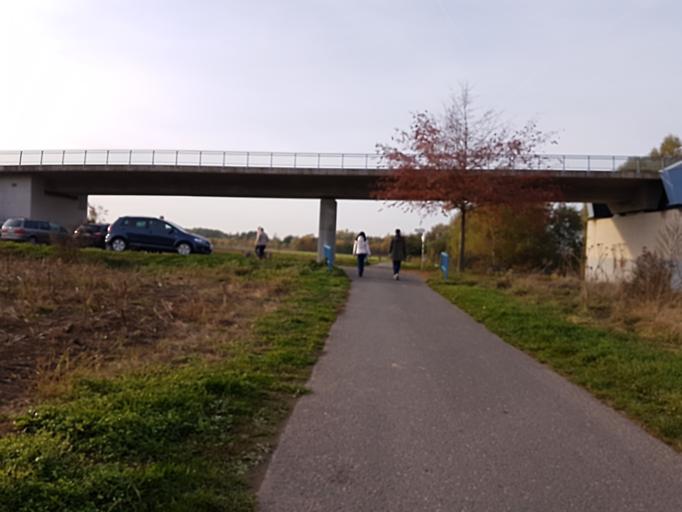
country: DE
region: Bavaria
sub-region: Regierungsbezirk Unterfranken
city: Sulzbach am Main
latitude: 49.8944
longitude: 9.1511
